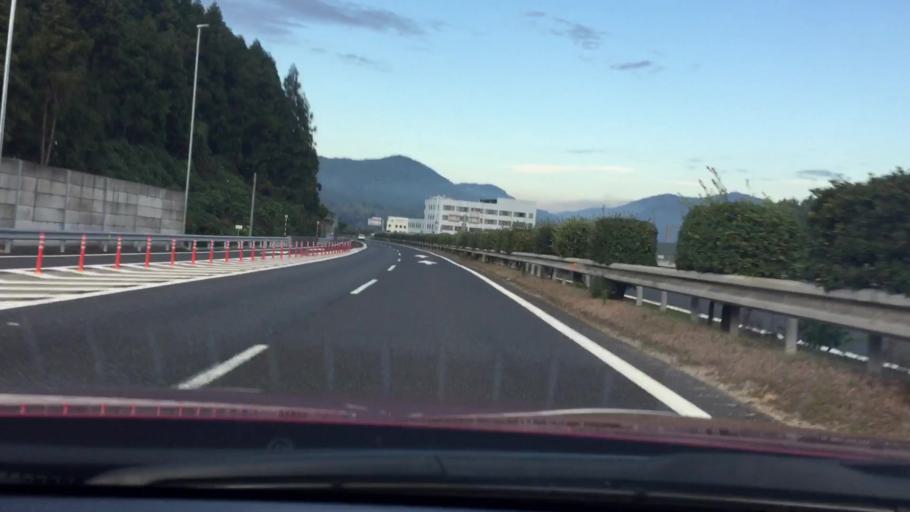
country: JP
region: Hyogo
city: Yamazakicho-nakabirose
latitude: 34.9633
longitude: 134.6916
